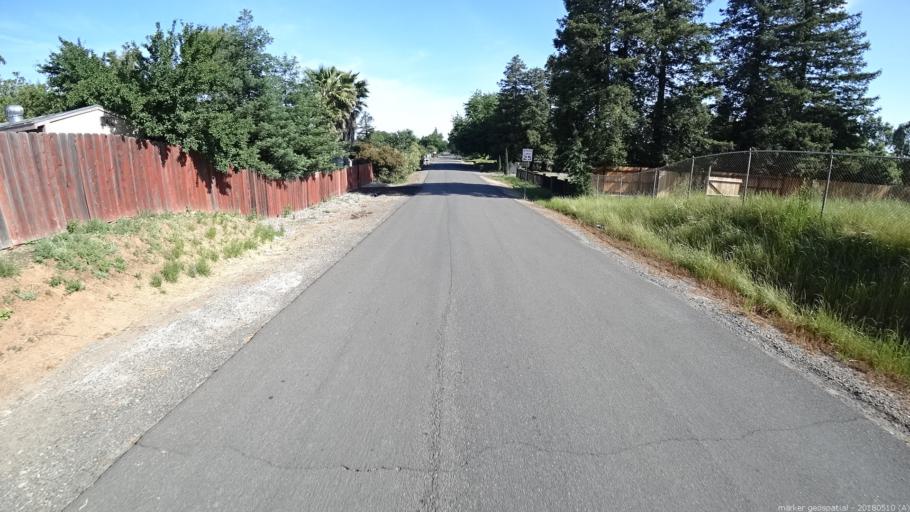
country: US
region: California
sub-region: Sacramento County
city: Rio Linda
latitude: 38.6568
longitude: -121.4777
